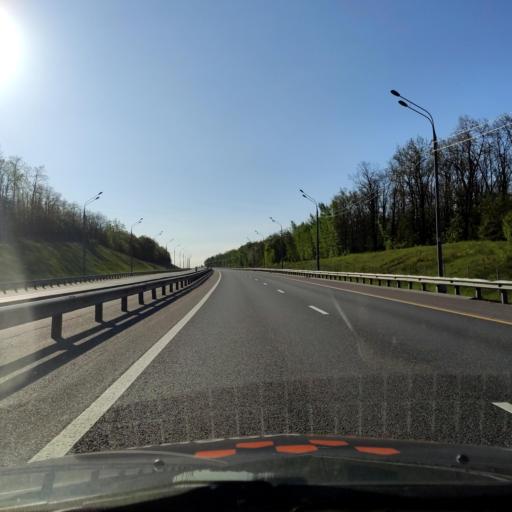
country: RU
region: Lipetsk
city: Khlevnoye
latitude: 52.2237
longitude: 39.1095
